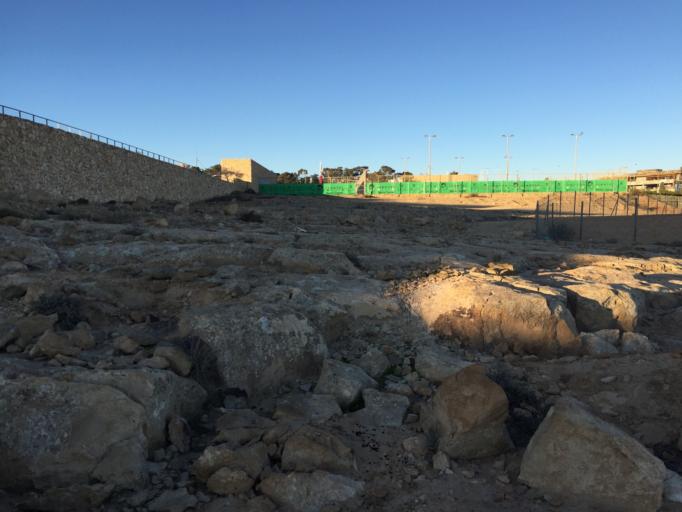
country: IL
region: Southern District
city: Mitzpe Ramon
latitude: 30.6129
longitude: 34.8067
